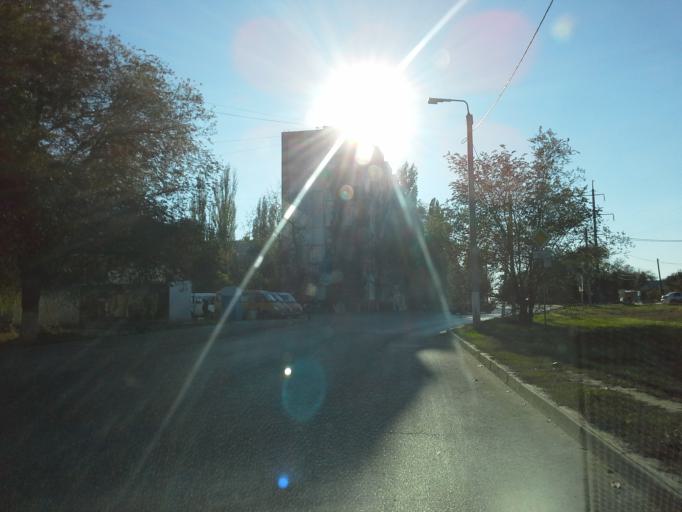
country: RU
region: Volgograd
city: Vodstroy
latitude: 48.8223
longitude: 44.6230
